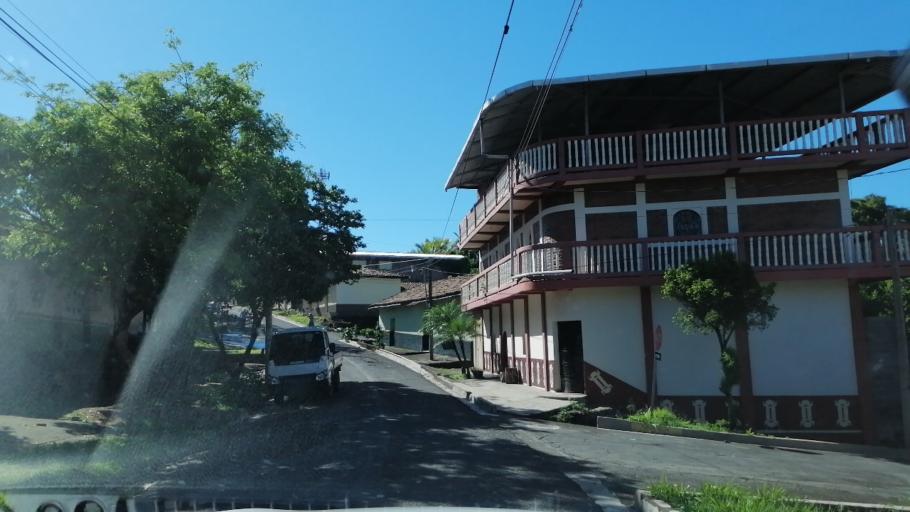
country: SV
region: Morazan
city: Corinto
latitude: 13.8090
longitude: -87.9720
